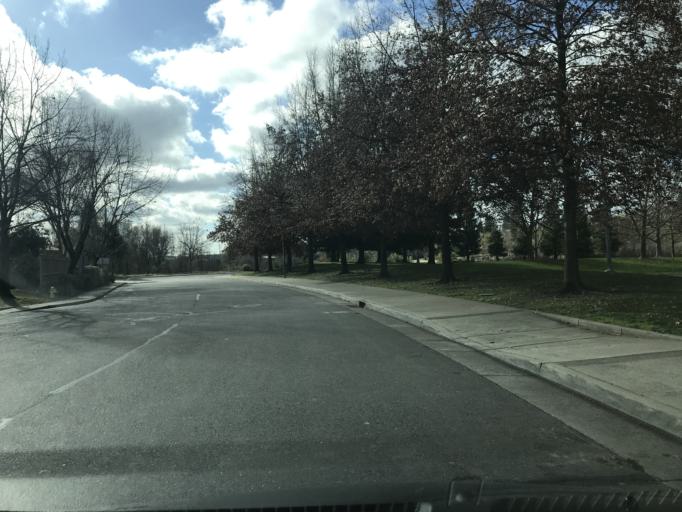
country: US
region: California
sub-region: Sacramento County
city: Folsom
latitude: 38.6524
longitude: -121.1342
